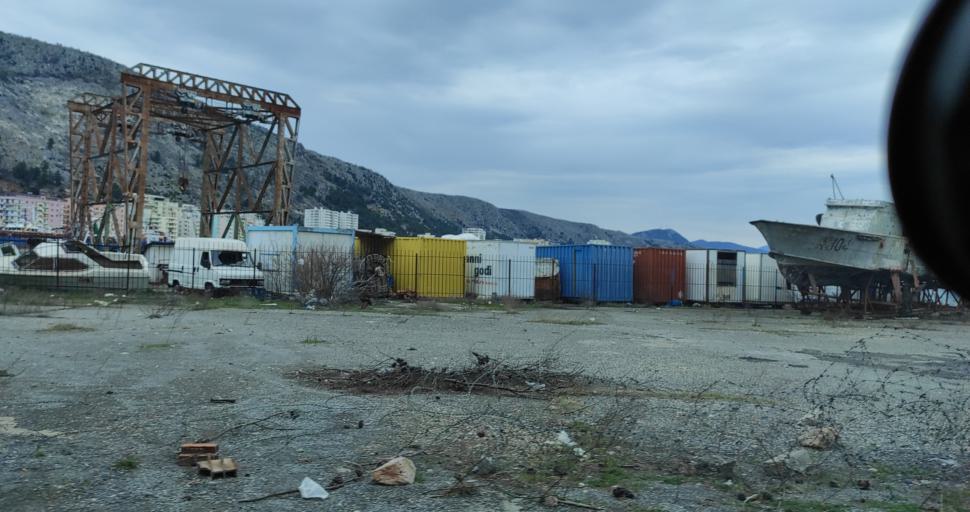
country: AL
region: Lezhe
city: Shengjin
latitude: 41.8126
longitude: 19.5854
